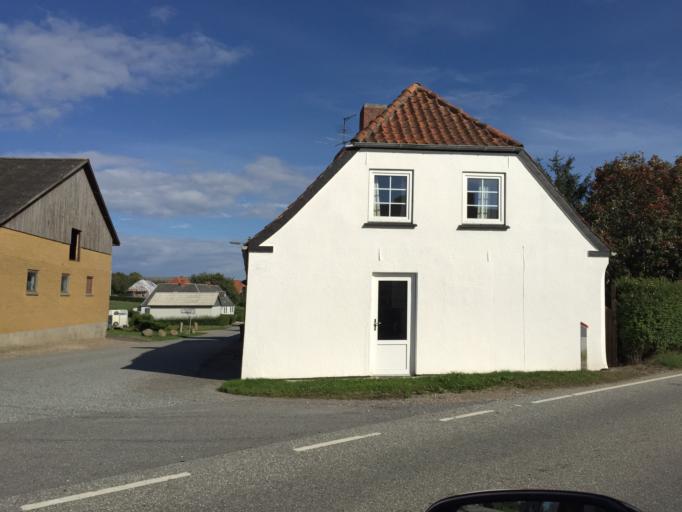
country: DK
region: South Denmark
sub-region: Sonderborg Kommune
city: Nordborg
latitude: 55.0247
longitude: 9.7911
